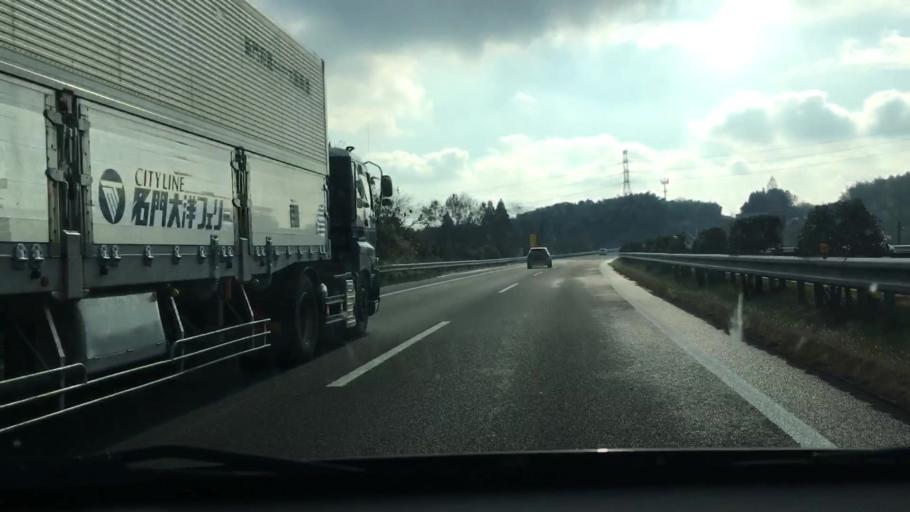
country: JP
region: Kumamoto
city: Uto
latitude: 32.6862
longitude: 130.7354
